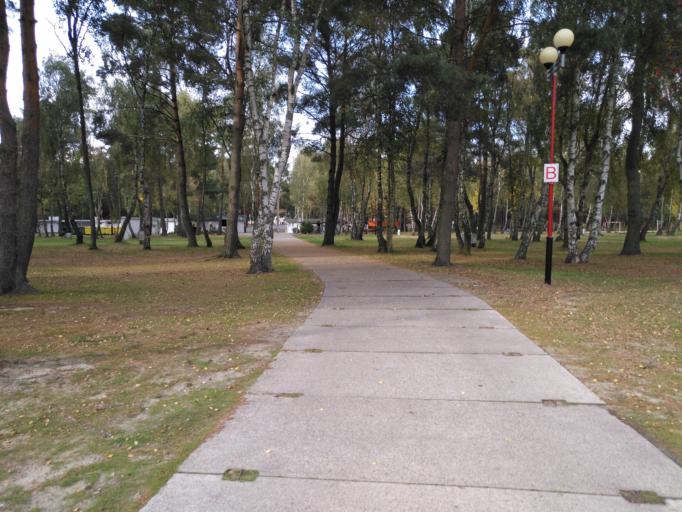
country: PL
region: West Pomeranian Voivodeship
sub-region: Powiat kolobrzeski
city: Grzybowo
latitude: 54.1607
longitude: 15.4262
